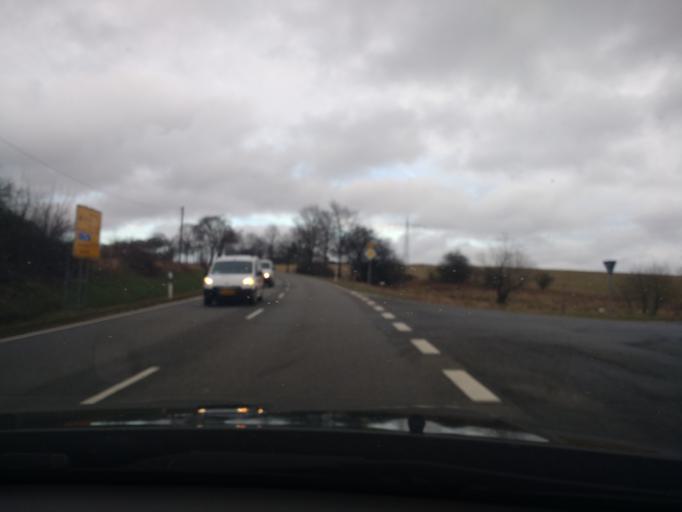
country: DE
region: Rheinland-Pfalz
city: Kell
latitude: 49.6359
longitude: 6.8372
